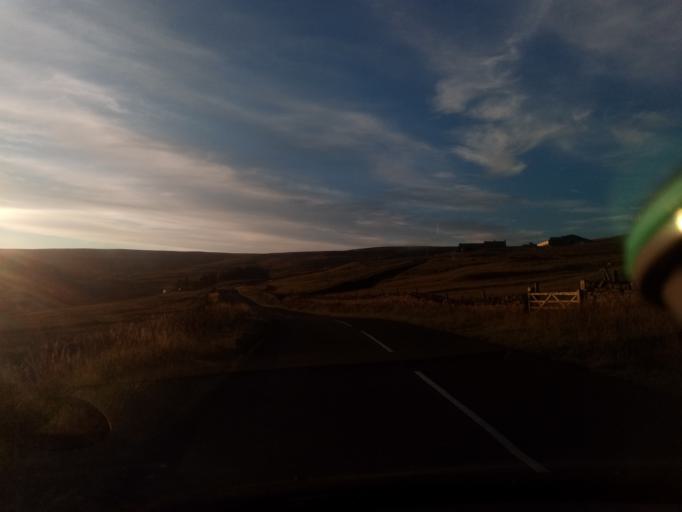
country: GB
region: England
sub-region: County Durham
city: Holwick
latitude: 54.7762
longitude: -2.2583
